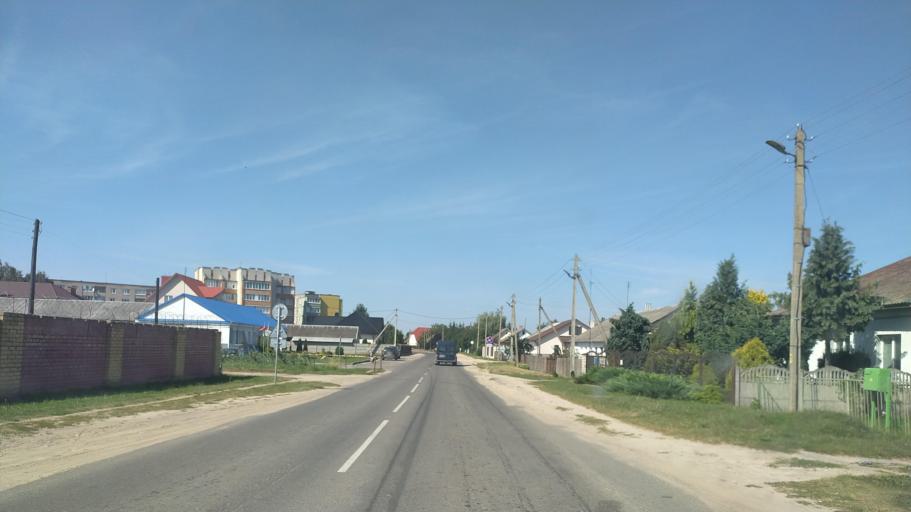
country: BY
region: Brest
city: Byaroza
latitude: 52.5267
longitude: 24.9887
